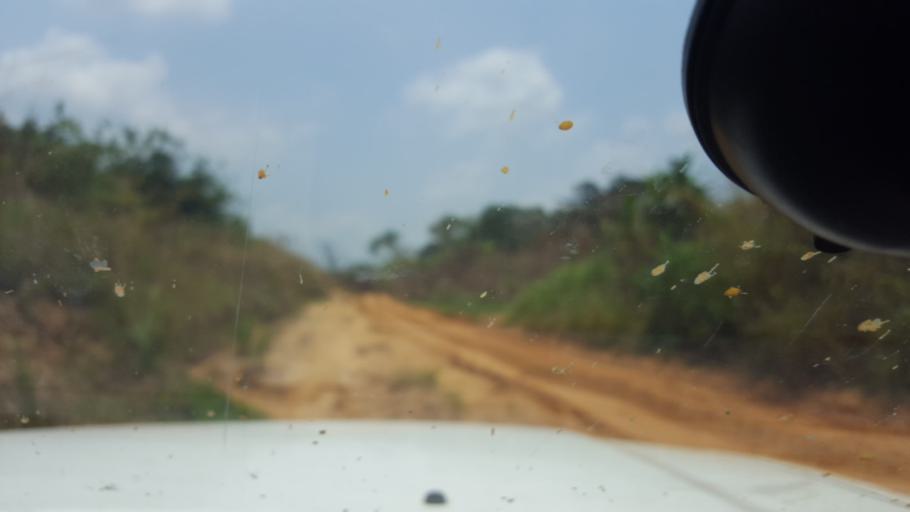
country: CD
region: Bandundu
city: Mushie
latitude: -3.7532
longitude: 16.6671
